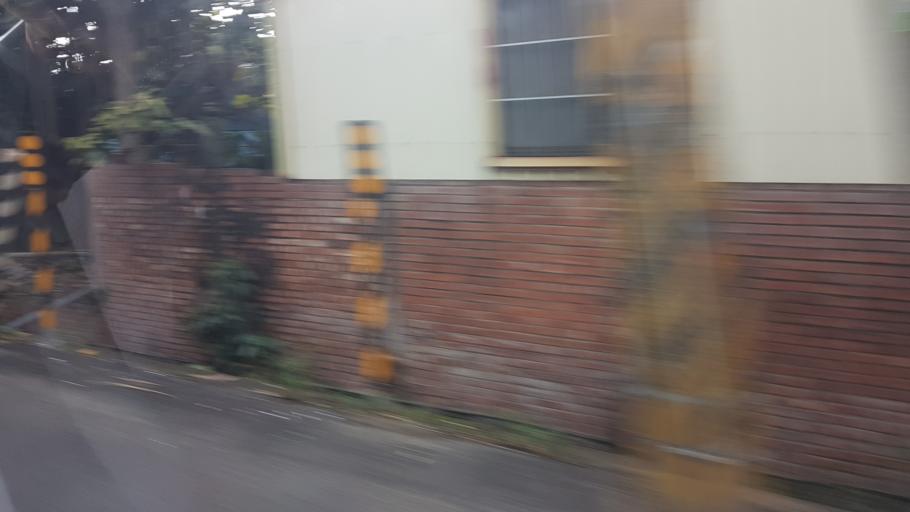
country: TW
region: Taiwan
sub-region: Chiayi
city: Jiayi Shi
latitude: 23.3798
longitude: 120.4389
